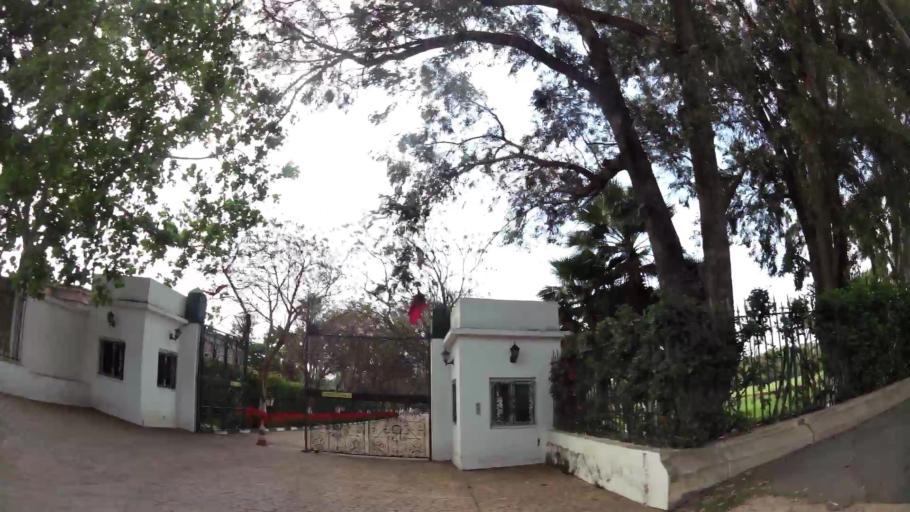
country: MA
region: Rabat-Sale-Zemmour-Zaer
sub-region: Rabat
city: Rabat
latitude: 33.9799
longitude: -6.8476
